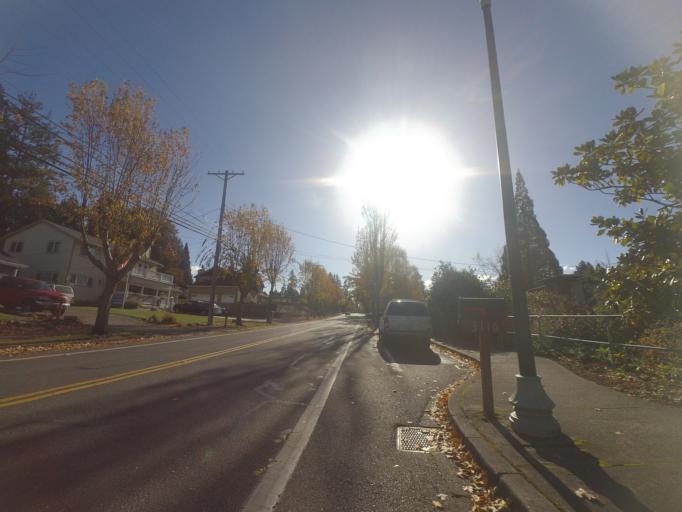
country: US
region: Washington
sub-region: Pierce County
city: University Place
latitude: 47.2311
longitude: -122.5505
